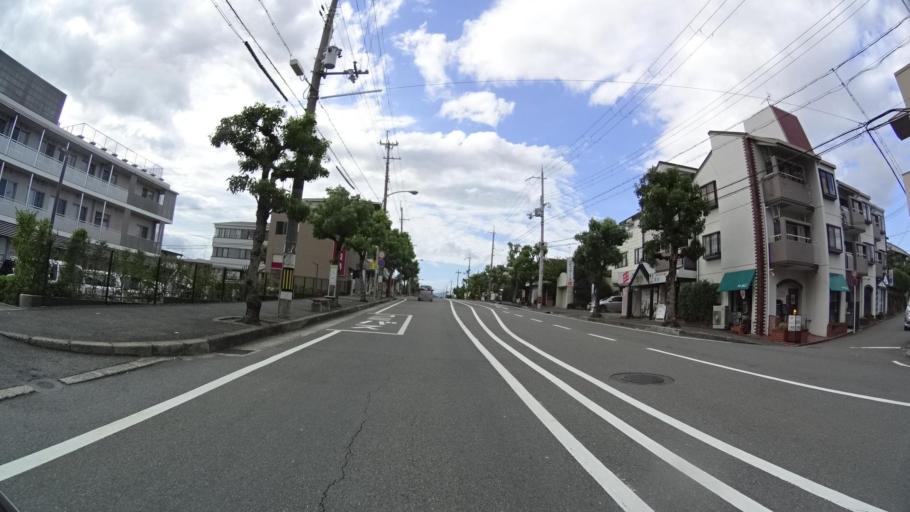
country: JP
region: Kyoto
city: Yawata
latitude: 34.8615
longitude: 135.6943
